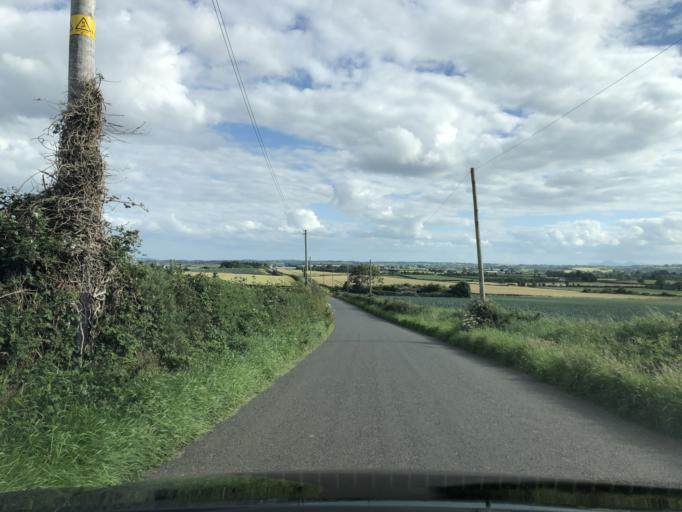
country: GB
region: Northern Ireland
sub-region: Ards District
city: Newtownards
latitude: 54.5685
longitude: -5.7128
